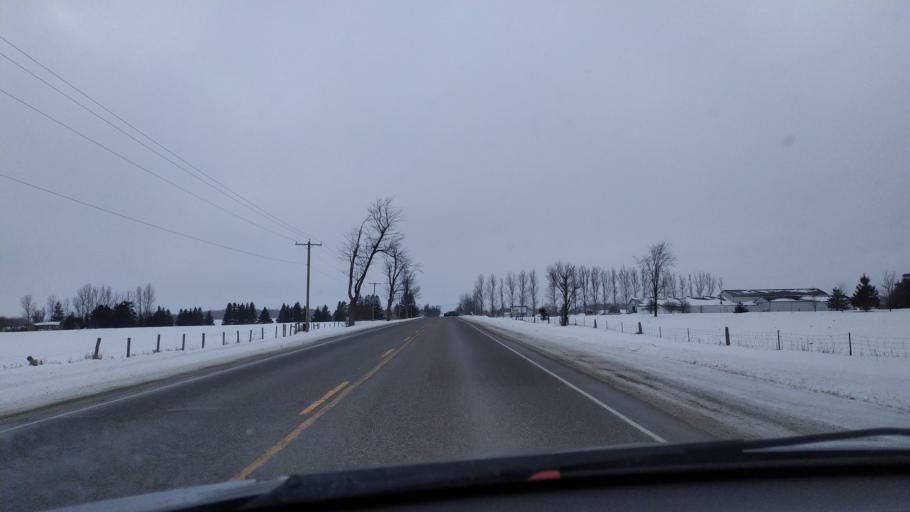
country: CA
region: Ontario
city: North Perth
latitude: 43.5940
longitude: -80.8884
